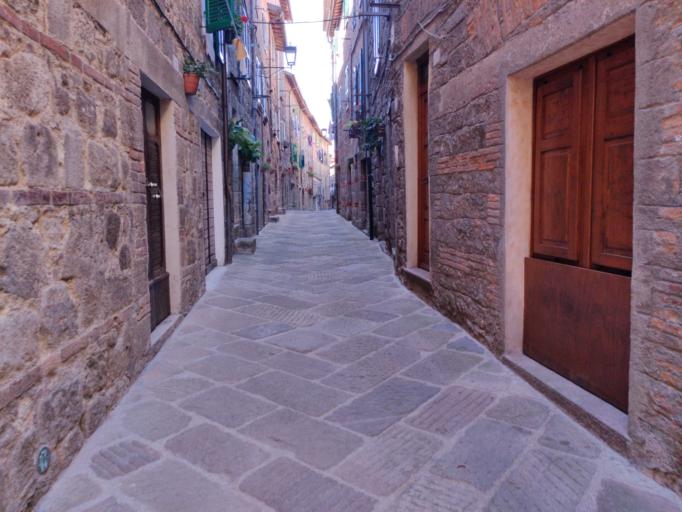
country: IT
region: Tuscany
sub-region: Provincia di Siena
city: Abbadia San Salvatore
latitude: 42.8805
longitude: 11.6783
